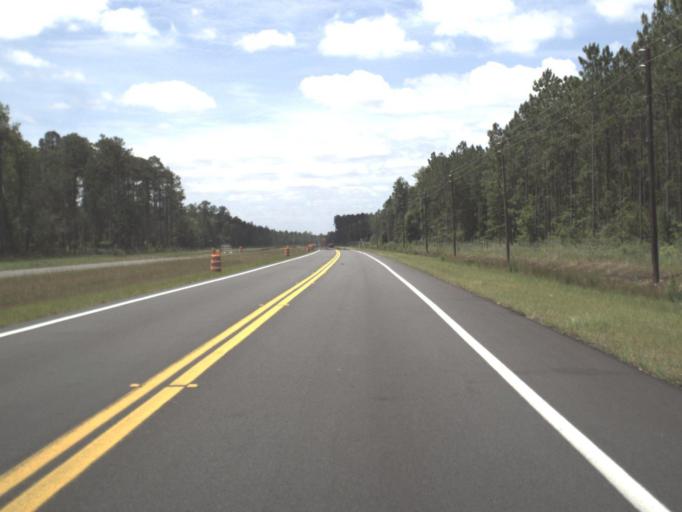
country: US
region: Florida
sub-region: Duval County
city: Baldwin
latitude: 30.4116
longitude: -81.9307
